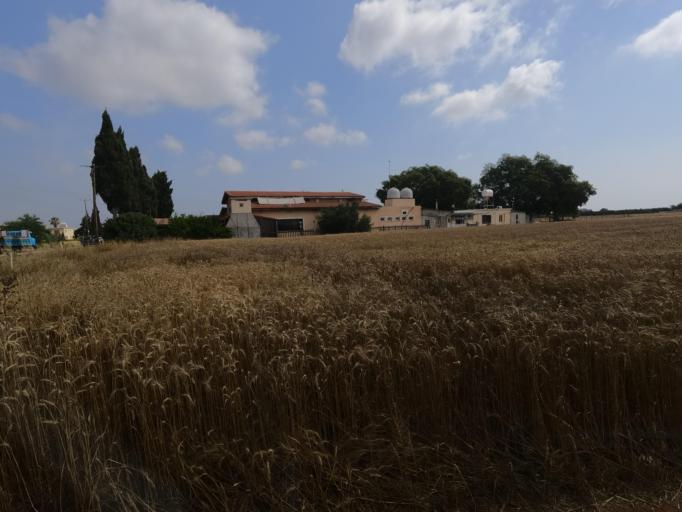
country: CY
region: Ammochostos
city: Deryneia
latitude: 35.0442
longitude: 33.9564
